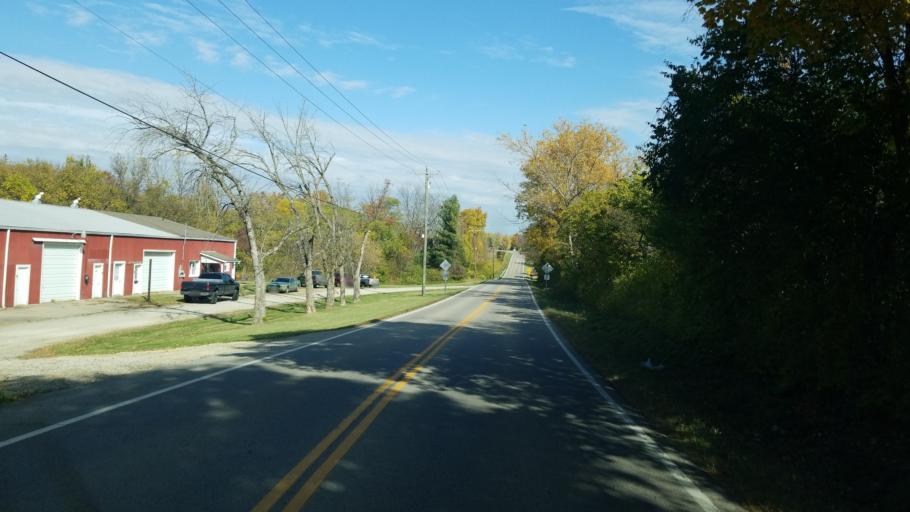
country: US
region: Ohio
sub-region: Warren County
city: Lebanon
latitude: 39.4056
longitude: -84.1800
